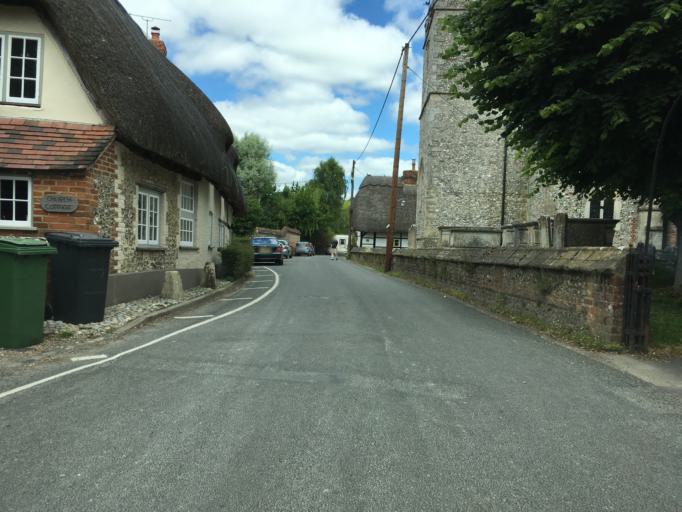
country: GB
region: England
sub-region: Hampshire
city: Highclere
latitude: 51.2501
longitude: -1.3961
